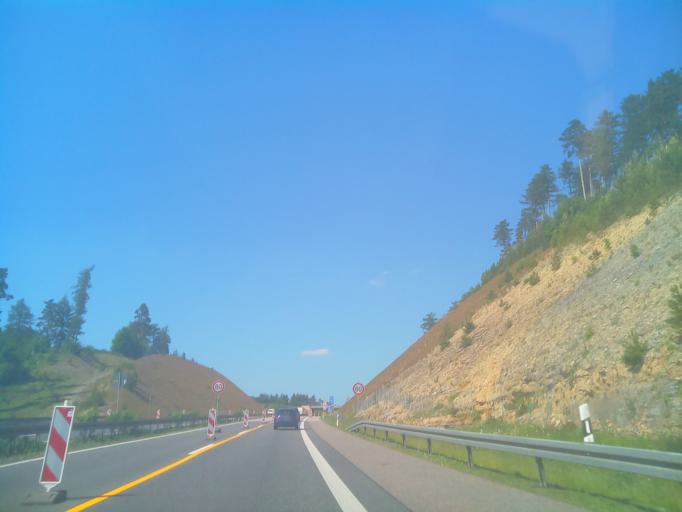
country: DE
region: Thuringia
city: Rohr
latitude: 50.5735
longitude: 10.4804
